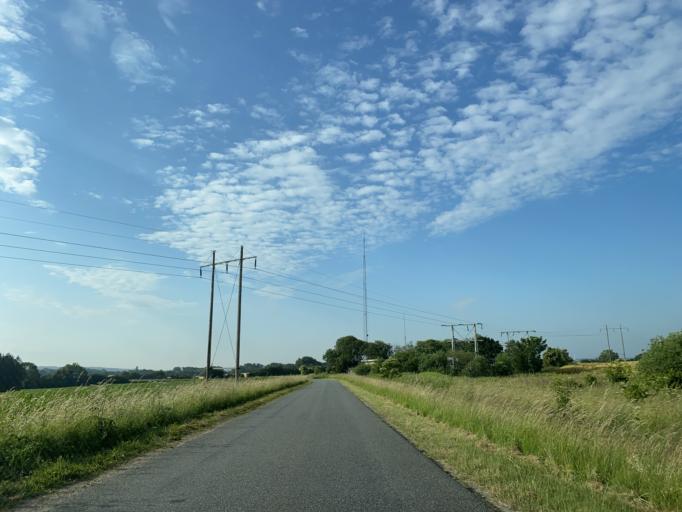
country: DK
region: South Denmark
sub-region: Haderslev Kommune
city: Haderslev
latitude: 55.1907
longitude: 9.4711
